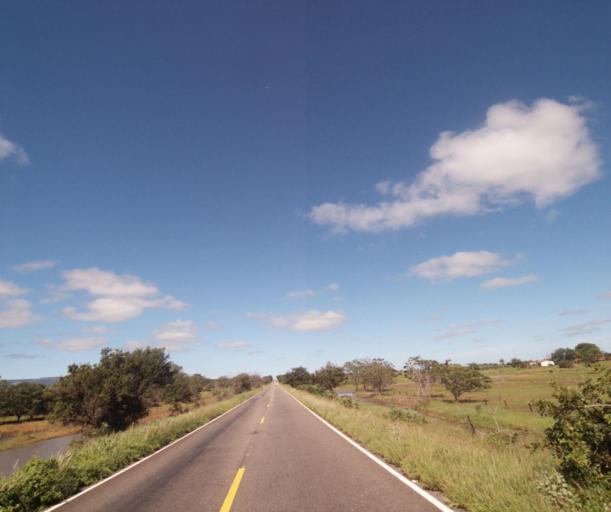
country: BR
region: Bahia
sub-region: Palmas De Monte Alto
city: Palmas de Monte Alto
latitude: -14.2384
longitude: -43.0232
